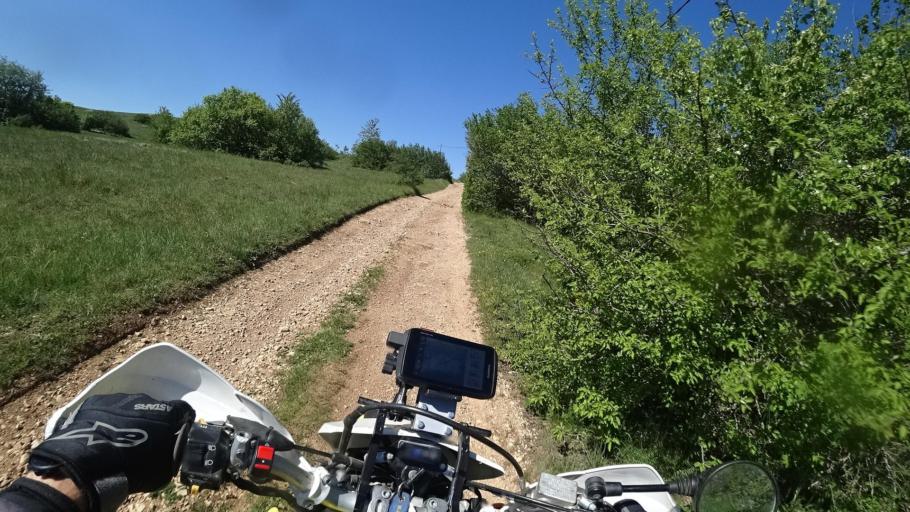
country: BA
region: Federation of Bosnia and Herzegovina
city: Rumboci
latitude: 43.8473
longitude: 17.5183
